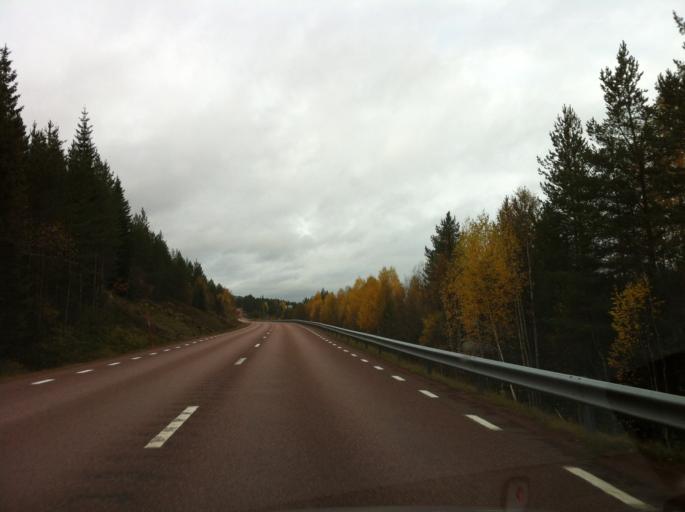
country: SE
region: Dalarna
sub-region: Alvdalens Kommun
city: AElvdalen
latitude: 61.2775
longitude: 13.7735
